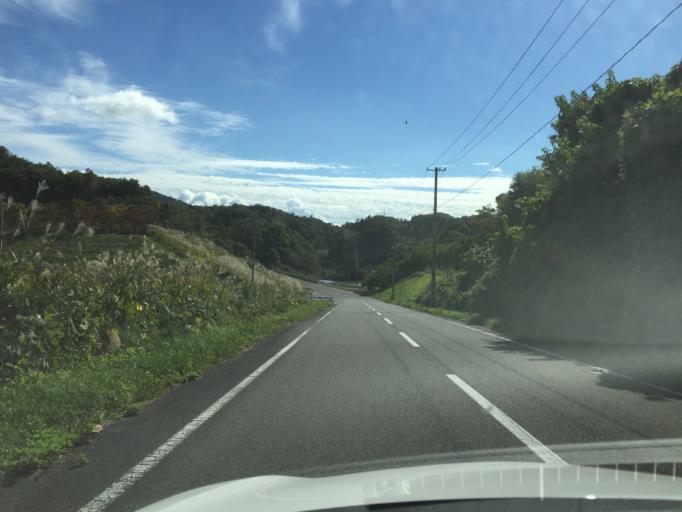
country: JP
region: Fukushima
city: Funehikimachi-funehiki
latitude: 37.4374
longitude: 140.5336
